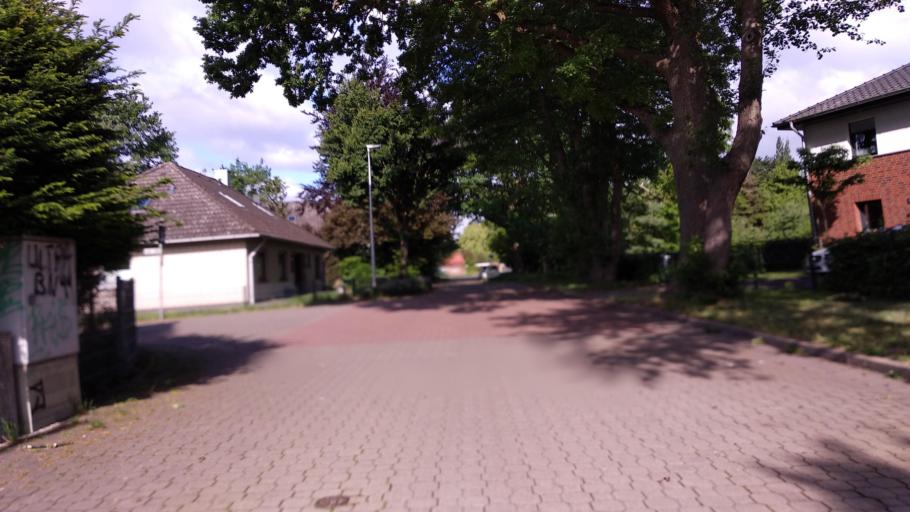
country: DE
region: Lower Saxony
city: Hagenburg
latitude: 52.4619
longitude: 9.3786
